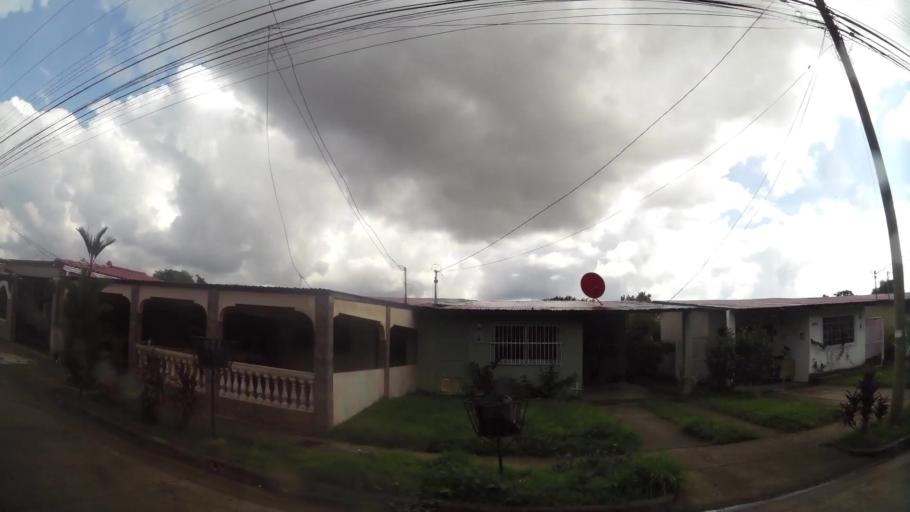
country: PA
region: Panama
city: Nuevo Arraijan
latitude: 8.9347
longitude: -79.7392
